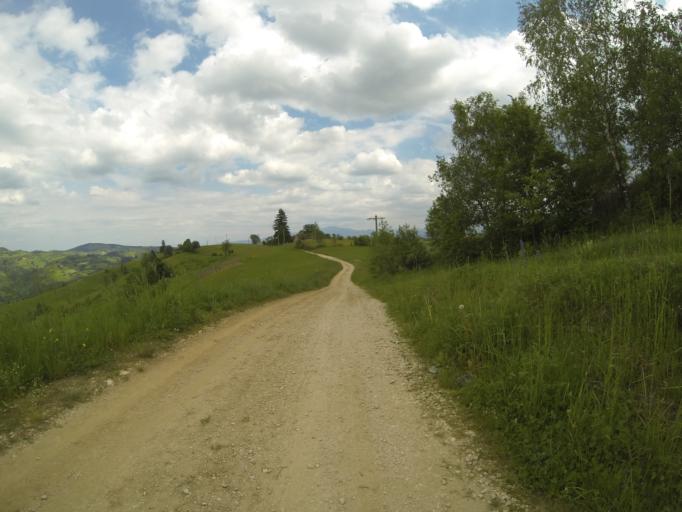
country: RO
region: Brasov
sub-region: Comuna Poiana Marului
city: Poiana Marului
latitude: 45.6338
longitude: 25.3037
